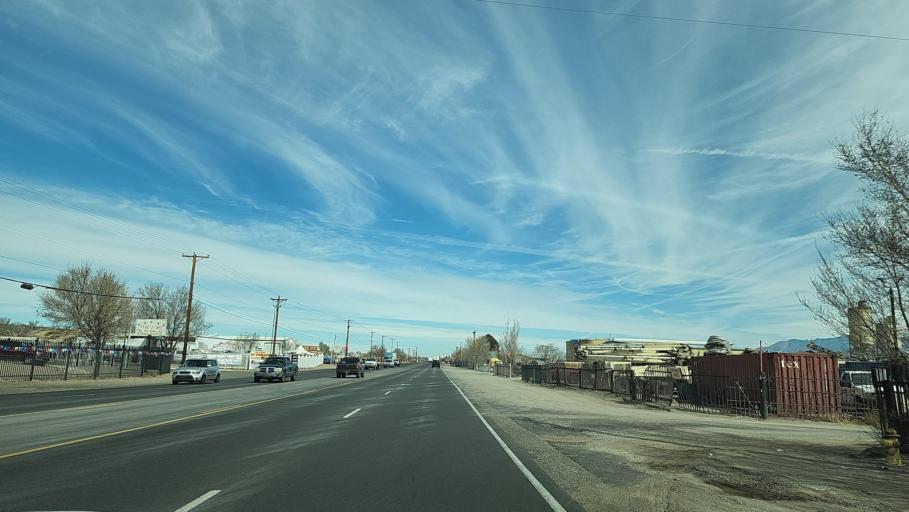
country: US
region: New Mexico
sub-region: Bernalillo County
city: South Valley
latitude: 35.0453
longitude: -106.7095
